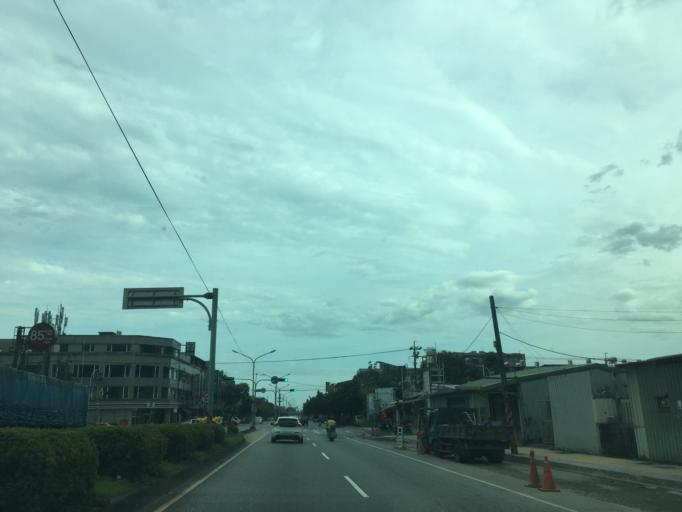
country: TW
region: Taiwan
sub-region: Hualien
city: Hualian
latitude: 24.0376
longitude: 121.6045
